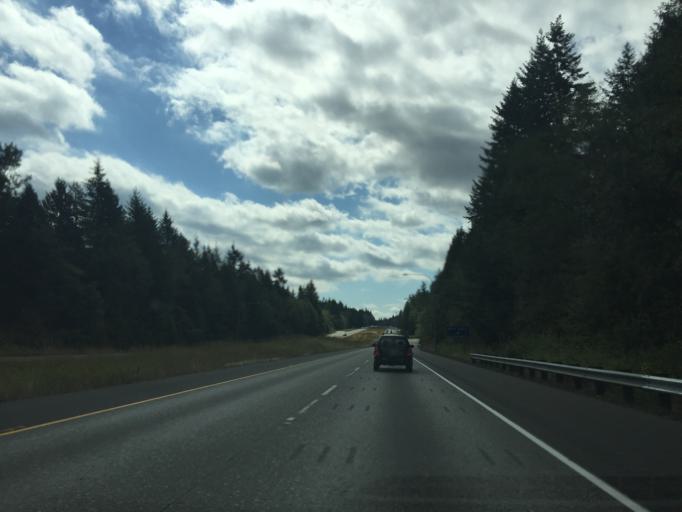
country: US
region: Washington
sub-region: Skagit County
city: Burlington
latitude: 48.5889
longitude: -122.3448
